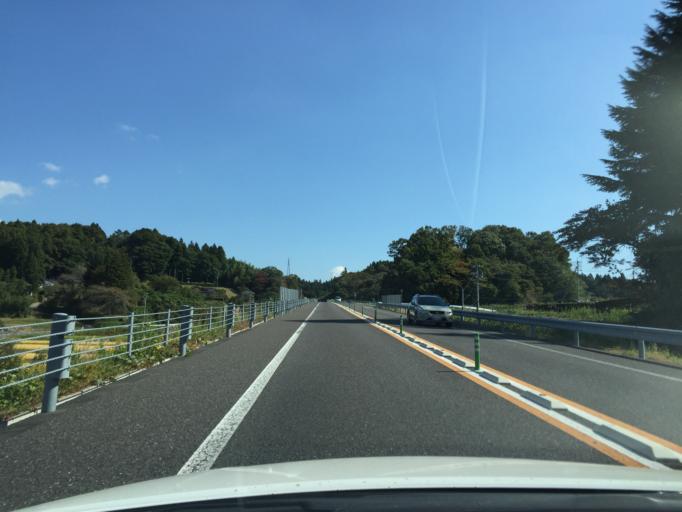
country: JP
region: Fukushima
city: Ishikawa
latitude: 37.2010
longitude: 140.4571
